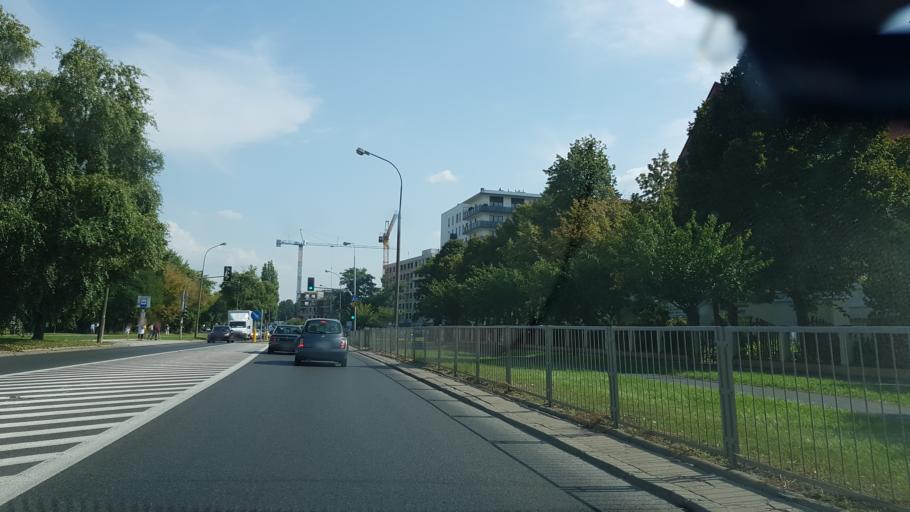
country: PL
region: Masovian Voivodeship
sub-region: Warszawa
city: Bielany
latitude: 52.2718
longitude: 20.9273
